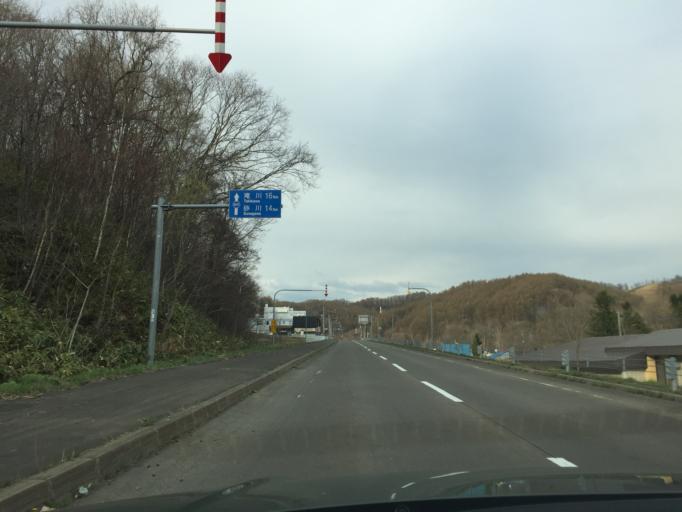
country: JP
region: Hokkaido
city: Utashinai
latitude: 43.5086
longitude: 142.0220
